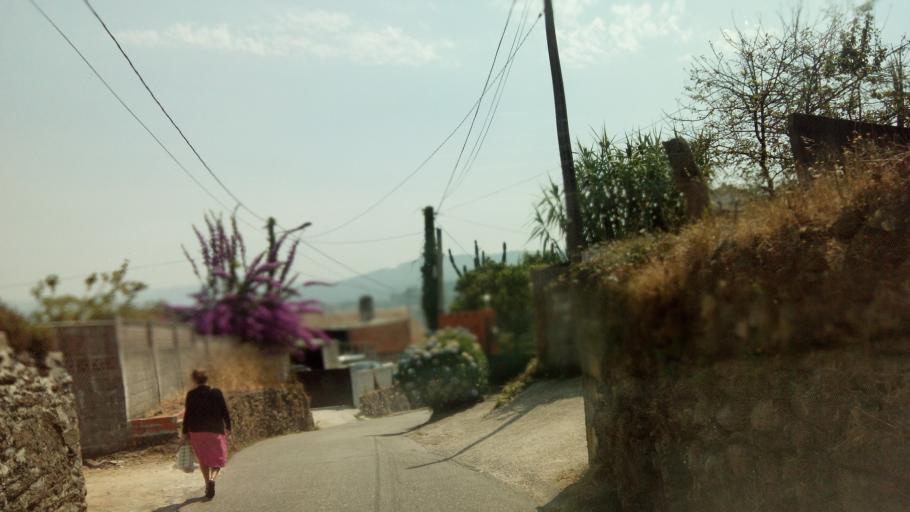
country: ES
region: Galicia
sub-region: Provincia de Pontevedra
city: Nigran
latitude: 42.1086
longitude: -8.8133
